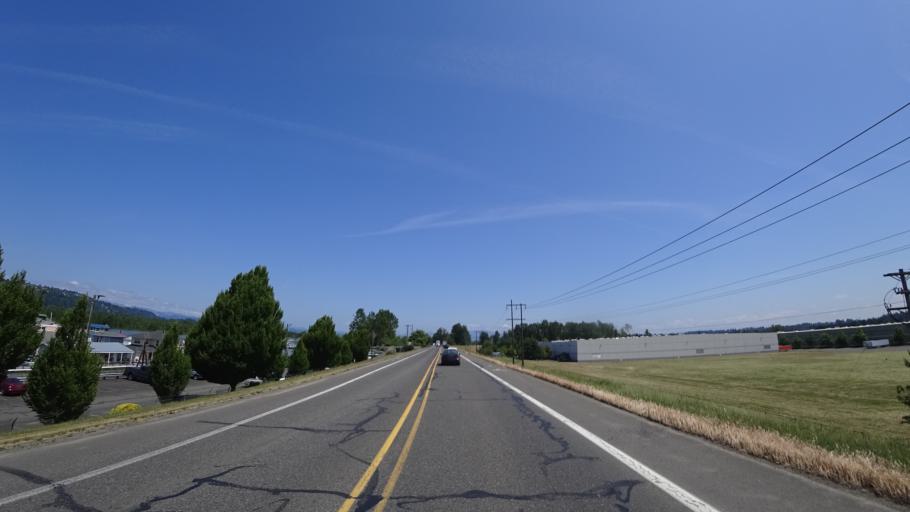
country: US
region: Oregon
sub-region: Multnomah County
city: Fairview
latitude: 45.5580
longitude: -122.4668
